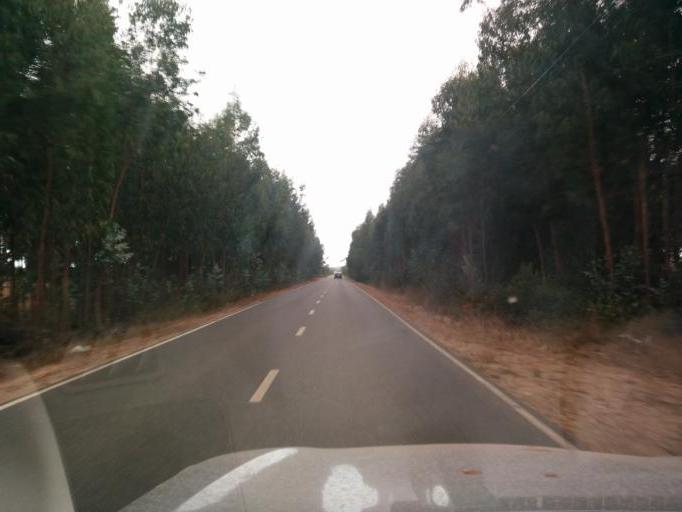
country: PT
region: Beja
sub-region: Odemira
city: Sao Teotonio
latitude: 37.5644
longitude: -8.7362
